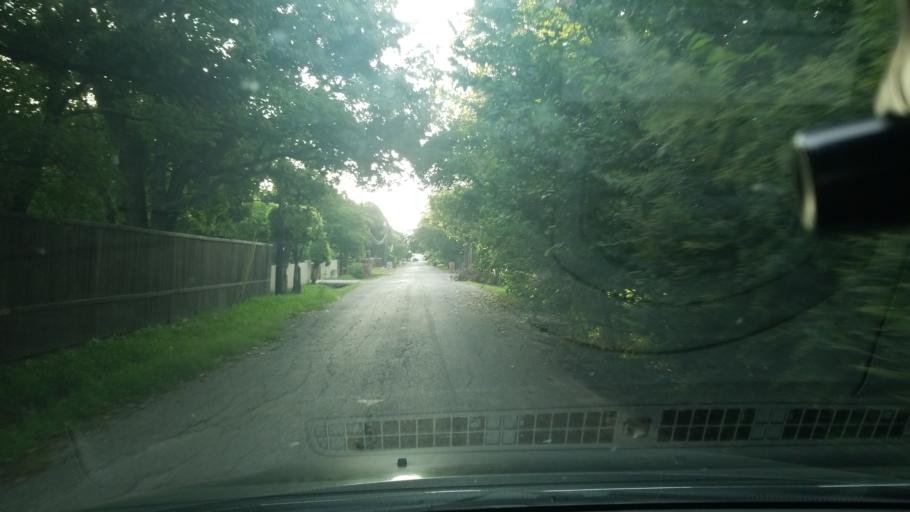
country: US
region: Texas
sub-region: Dallas County
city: Balch Springs
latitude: 32.7459
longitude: -96.6374
